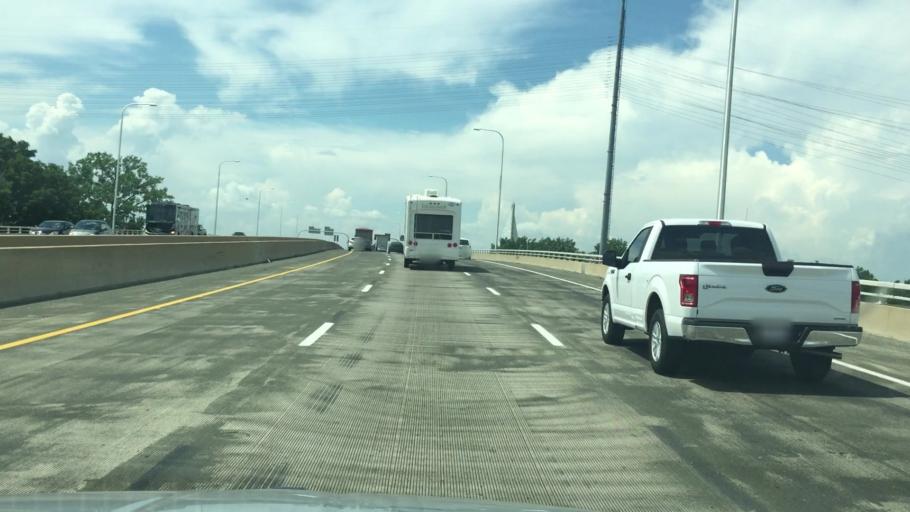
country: US
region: Ohio
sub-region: Lucas County
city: Oregon
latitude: 41.6520
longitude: -83.5034
